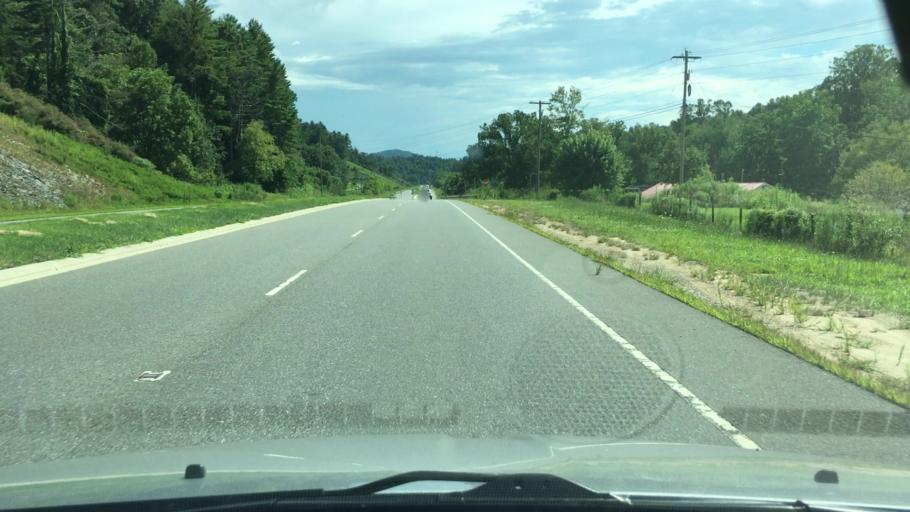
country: US
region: North Carolina
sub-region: Madison County
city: Mars Hill
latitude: 35.8698
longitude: -82.4824
